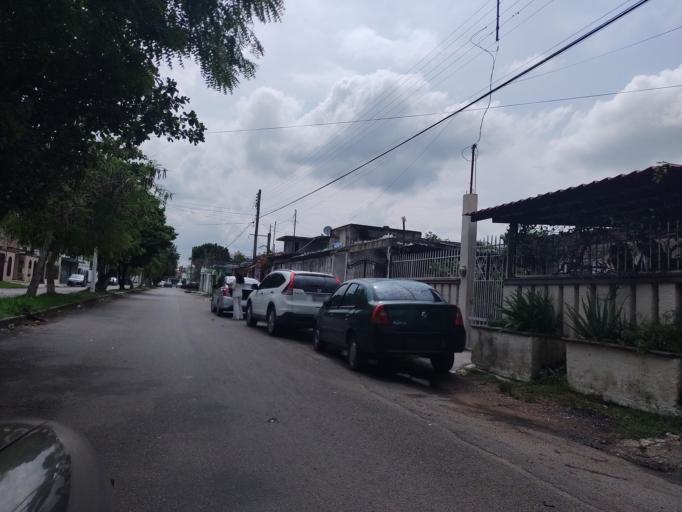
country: MX
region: Quintana Roo
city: Chetumal
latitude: 18.5170
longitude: -88.3127
